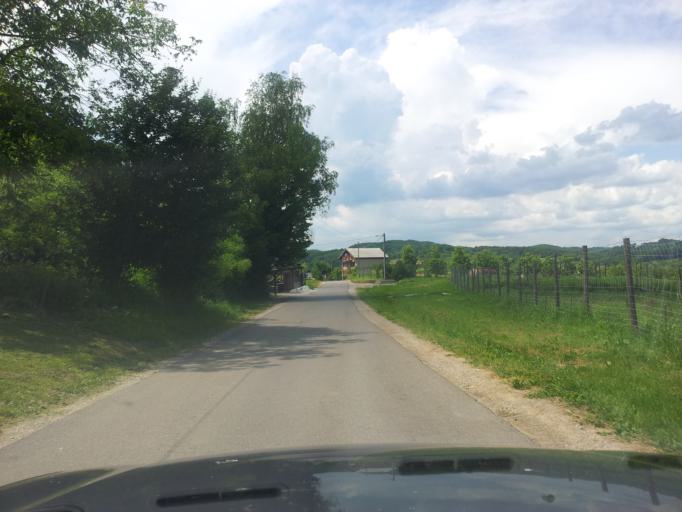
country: HR
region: Karlovacka
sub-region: Grad Karlovac
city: Karlovac
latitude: 45.4602
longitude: 15.5087
